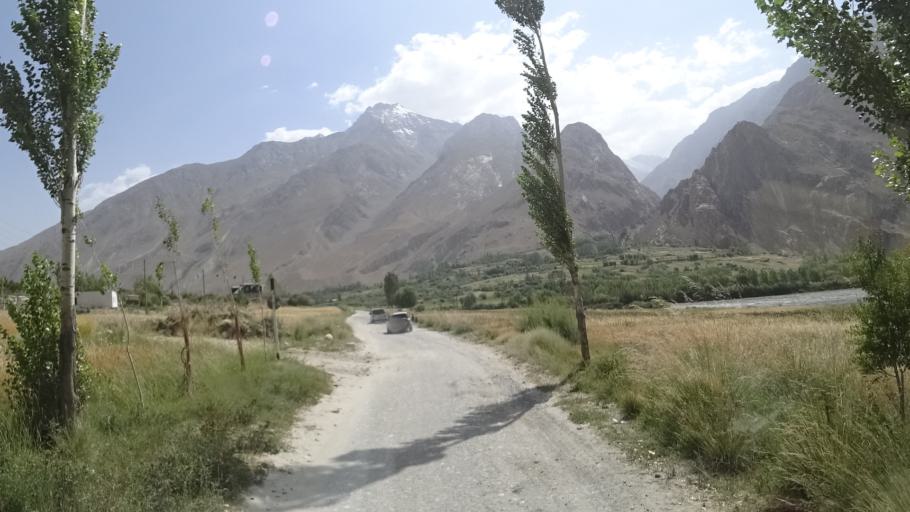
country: TJ
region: Gorno-Badakhshan
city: Ishqoshim
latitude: 36.9253
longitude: 71.4929
